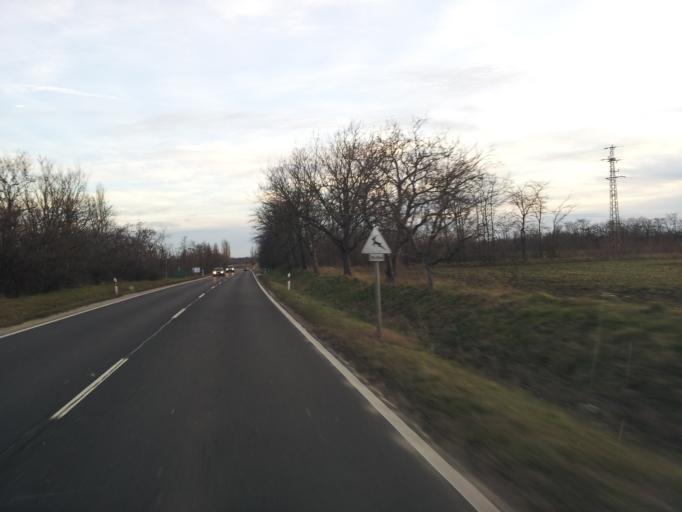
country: HU
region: Fejer
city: Lepseny
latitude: 47.0016
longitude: 18.1782
